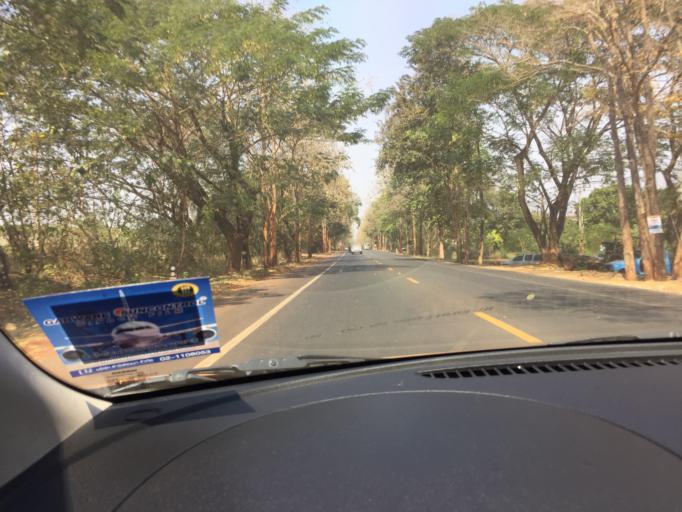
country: TH
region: Kanchanaburi
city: Sai Yok
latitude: 14.1666
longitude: 99.1335
